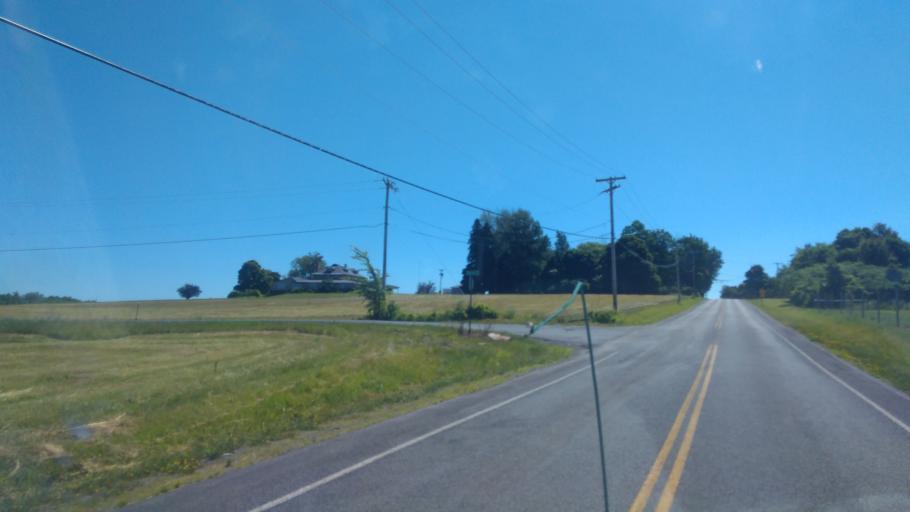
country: US
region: New York
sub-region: Wayne County
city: Sodus
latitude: 43.2726
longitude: -77.1002
